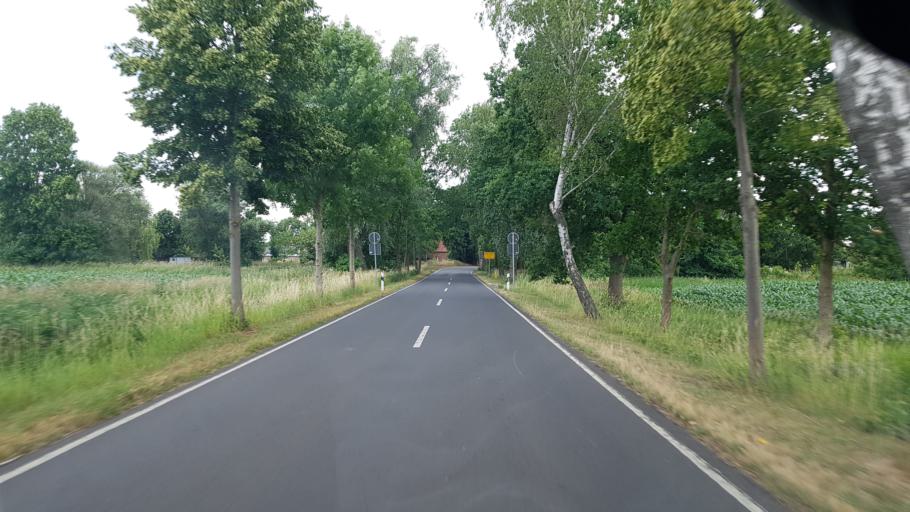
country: DE
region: Brandenburg
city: Kasel-Golzig
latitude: 51.9613
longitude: 13.6728
